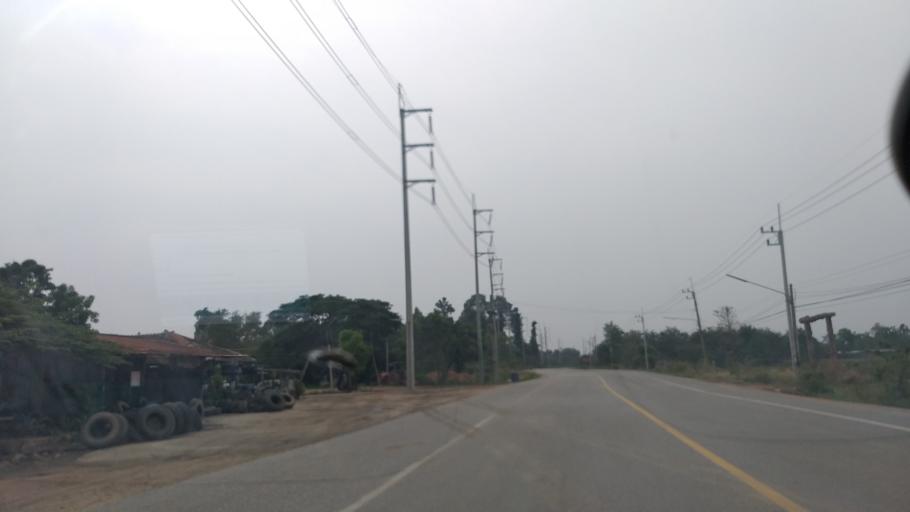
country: TH
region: Chachoengsao
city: Plaeng Yao
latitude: 13.5700
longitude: 101.2661
